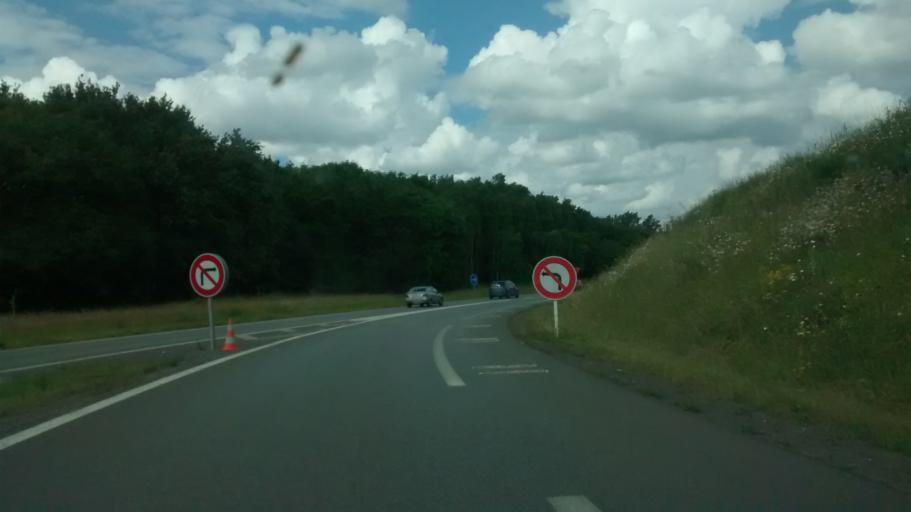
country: FR
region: Brittany
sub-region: Departement d'Ille-et-Vilaine
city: Saint-Jacques-de-la-Lande
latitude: 48.0772
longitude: -1.6940
